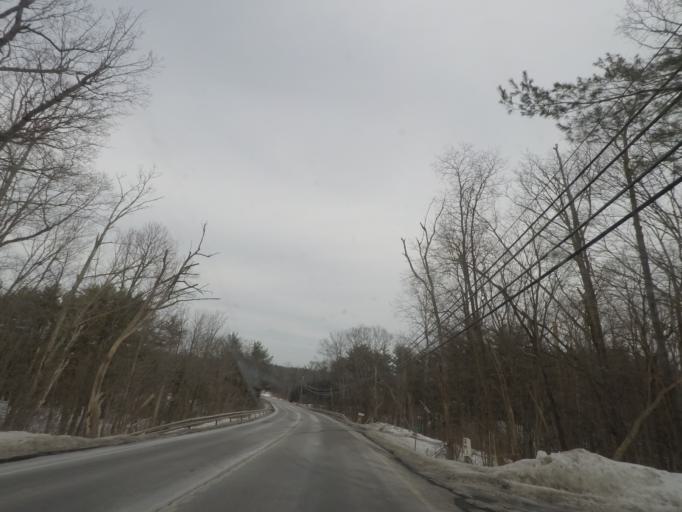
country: US
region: New York
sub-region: Albany County
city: Voorheesville
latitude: 42.5737
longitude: -73.9480
